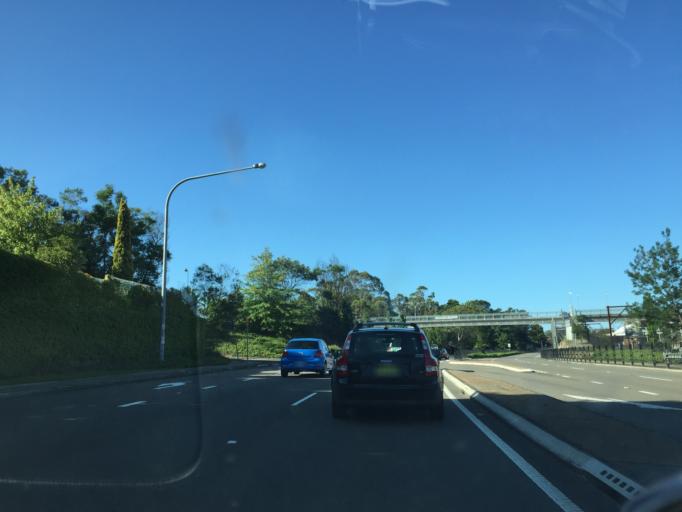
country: AU
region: New South Wales
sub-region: Blue Mountains Municipality
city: Hazelbrook
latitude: -33.6974
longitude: 150.5341
